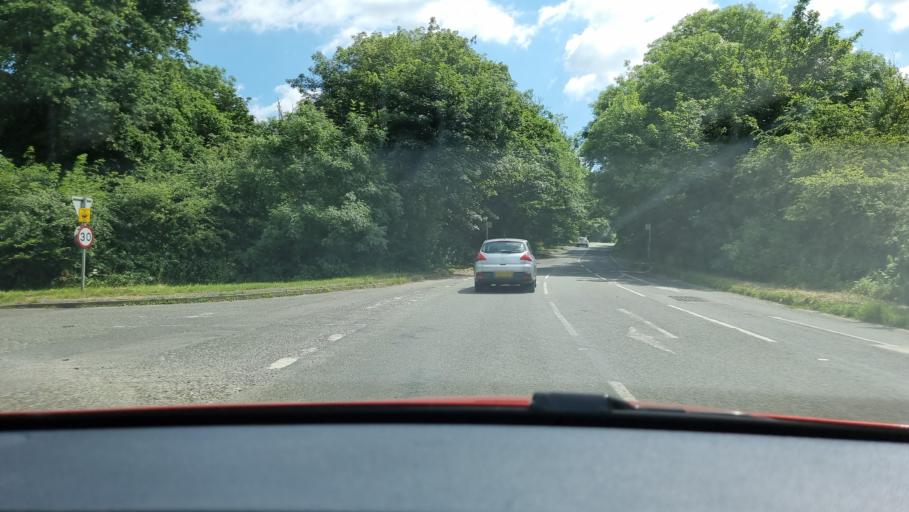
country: GB
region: England
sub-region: Oxfordshire
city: Kidlington
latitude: 51.8471
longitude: -1.3115
